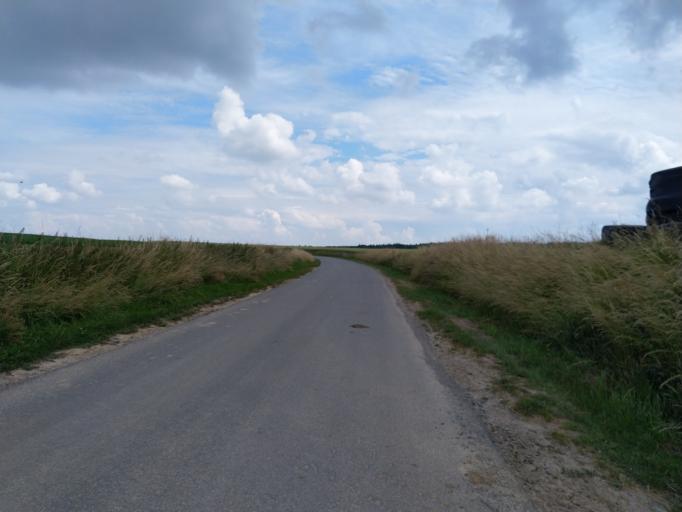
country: FR
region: Nord-Pas-de-Calais
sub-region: Departement du Nord
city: Boussois
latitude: 50.3486
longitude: 4.0227
